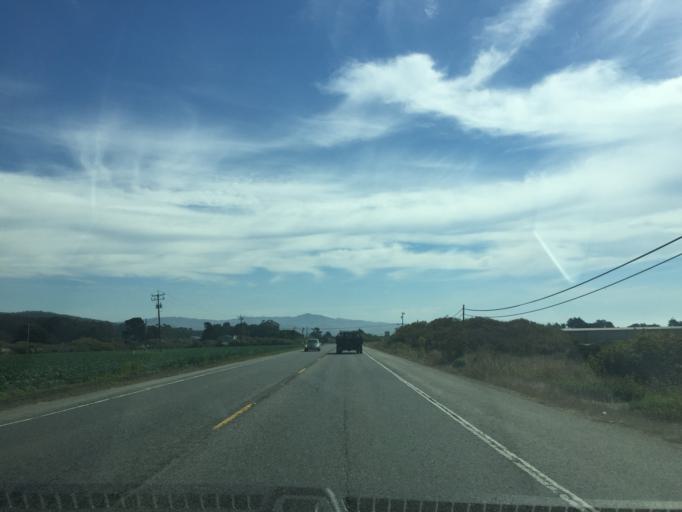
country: US
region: California
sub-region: San Mateo County
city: El Granada
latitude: 37.5126
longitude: -122.4919
